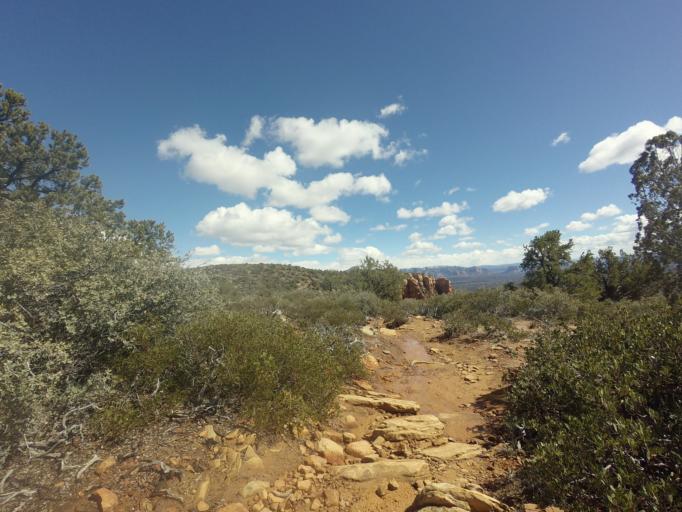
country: US
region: Arizona
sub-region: Yavapai County
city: West Sedona
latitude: 34.9038
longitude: -111.8752
